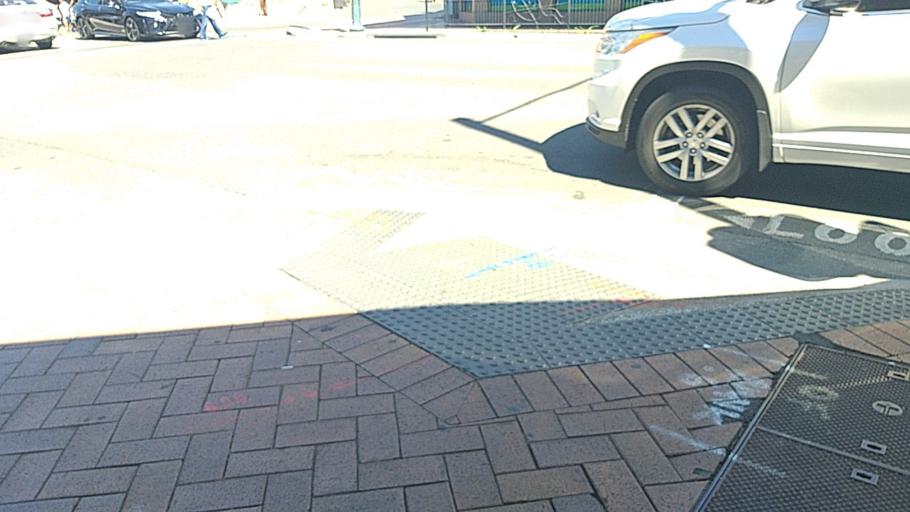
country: AU
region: New South Wales
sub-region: Fairfield
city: Liverpool
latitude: -33.9246
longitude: 150.9221
